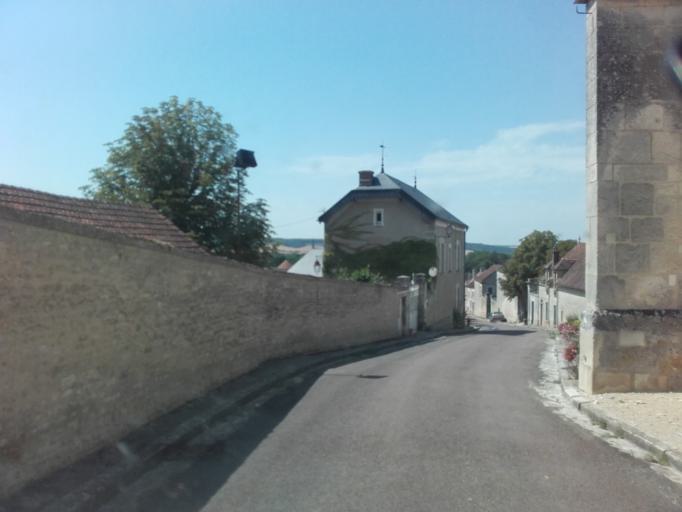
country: FR
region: Bourgogne
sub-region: Departement de l'Yonne
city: Chablis
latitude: 47.7644
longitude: 3.8942
